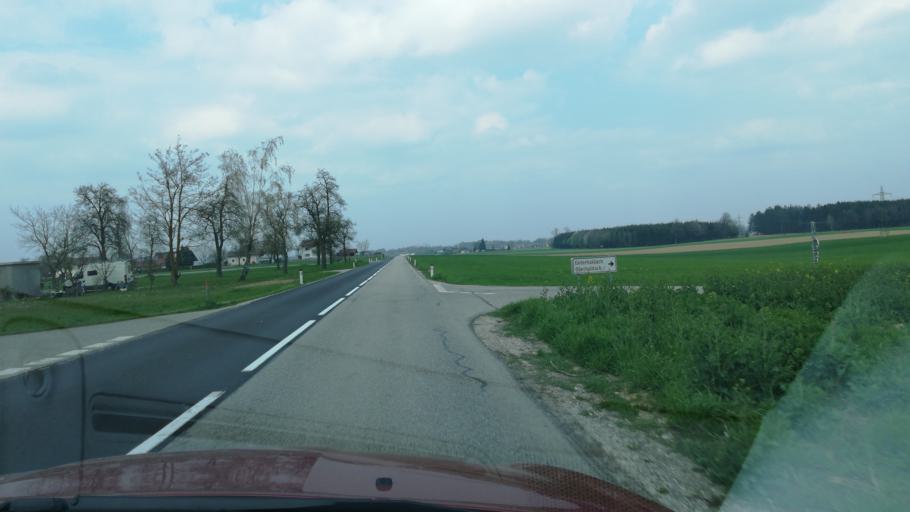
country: AT
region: Upper Austria
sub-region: Politischer Bezirk Vocklabruck
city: Desselbrunn
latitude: 48.0092
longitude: 13.7541
